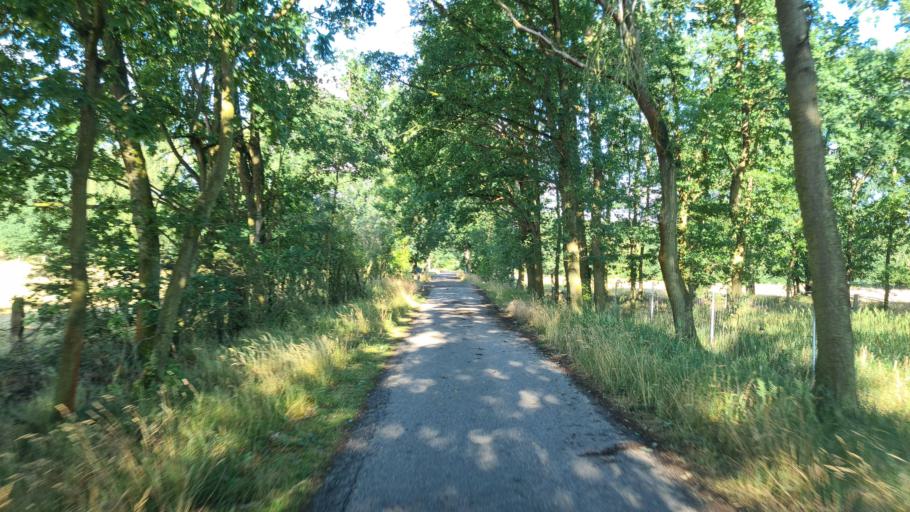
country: DE
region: Saxony
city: Beilrode
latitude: 51.6426
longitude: 13.0946
